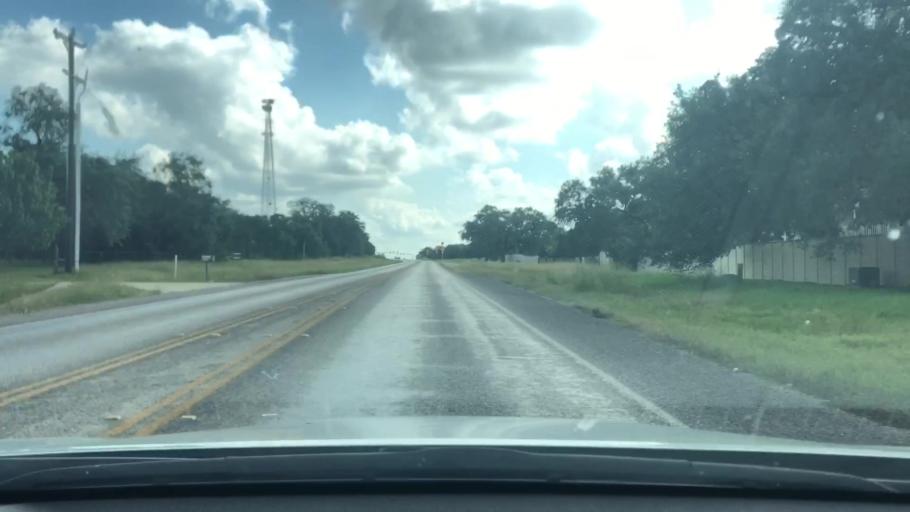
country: US
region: Texas
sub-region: Bexar County
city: Fair Oaks Ranch
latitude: 29.7365
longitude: -98.6233
